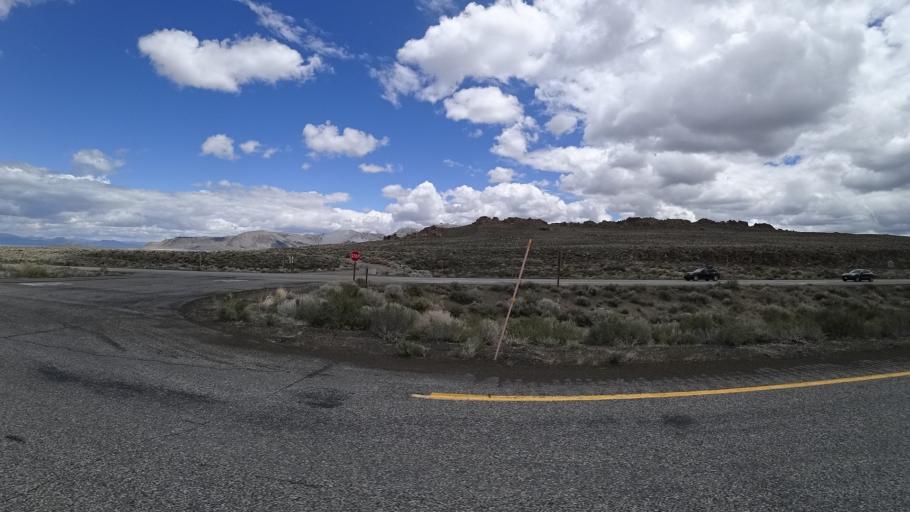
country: US
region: California
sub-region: Mono County
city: Mammoth Lakes
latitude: 37.8639
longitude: -119.0869
